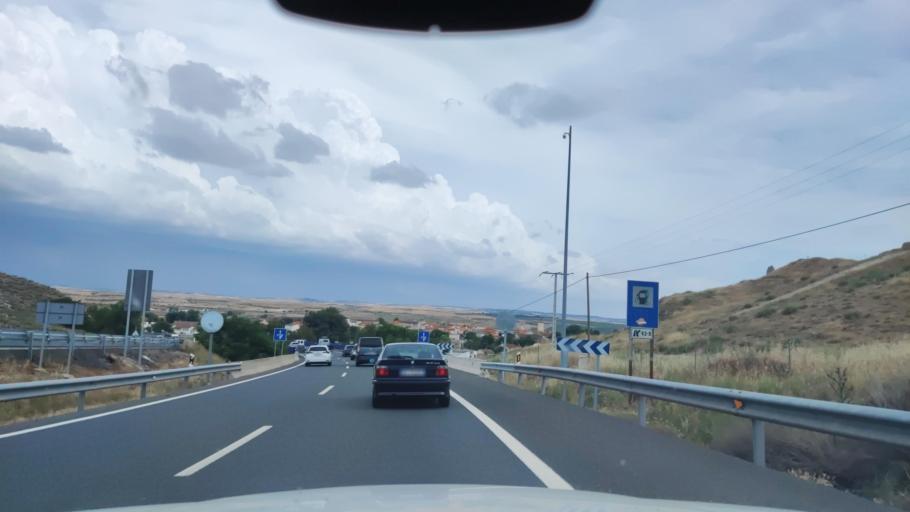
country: ES
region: Madrid
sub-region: Provincia de Madrid
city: Fuentiduena de Tajo
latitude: 40.1237
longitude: -3.1628
